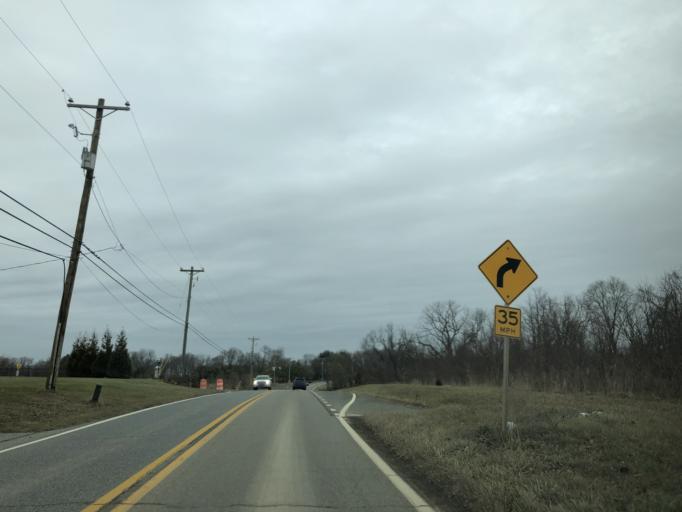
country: US
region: Delaware
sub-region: New Castle County
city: Middletown
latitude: 39.4877
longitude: -75.6944
